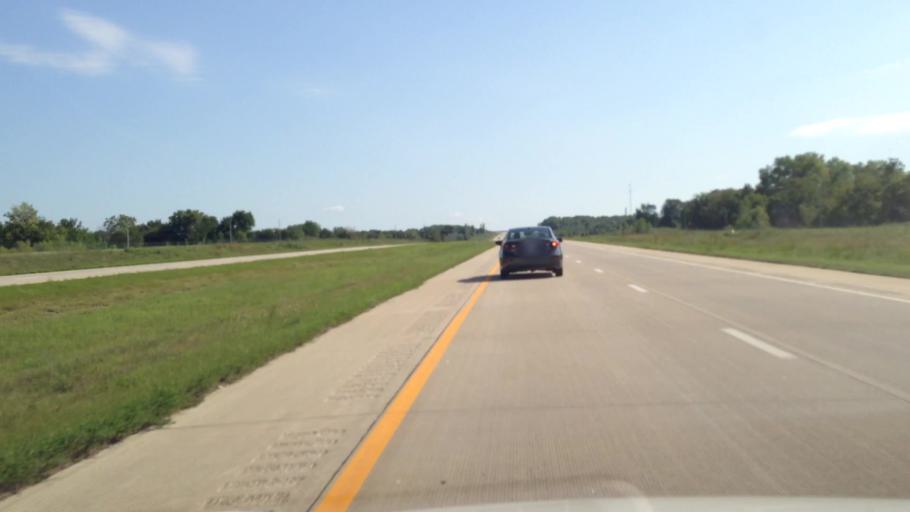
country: US
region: Kansas
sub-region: Linn County
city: Pleasanton
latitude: 38.1287
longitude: -94.7123
